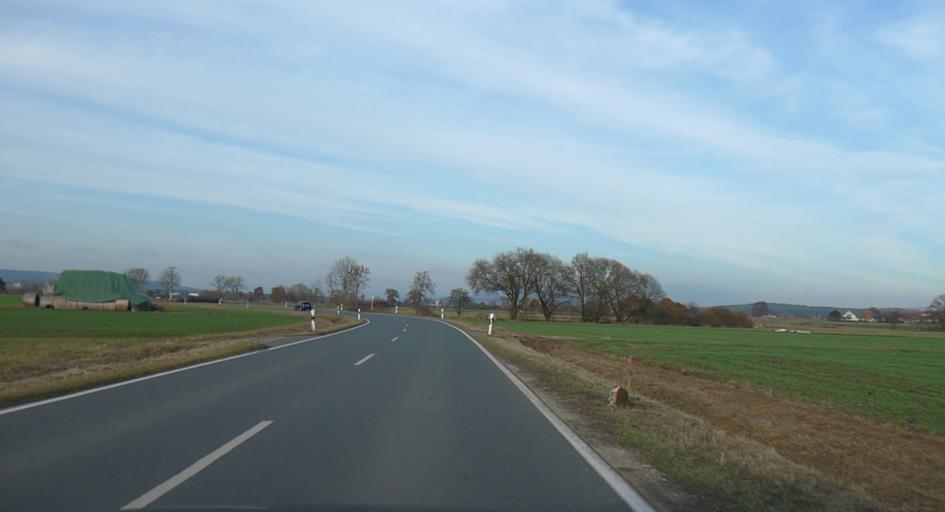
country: DE
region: Bavaria
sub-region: Regierungsbezirk Mittelfranken
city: Baiersdorf
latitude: 49.6520
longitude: 11.0470
